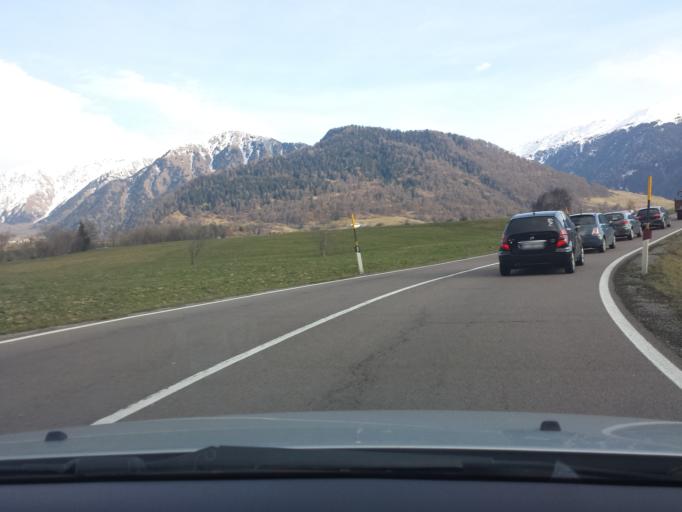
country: IT
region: Trentino-Alto Adige
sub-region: Bolzano
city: Malles Venosta
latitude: 46.7257
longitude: 10.5334
